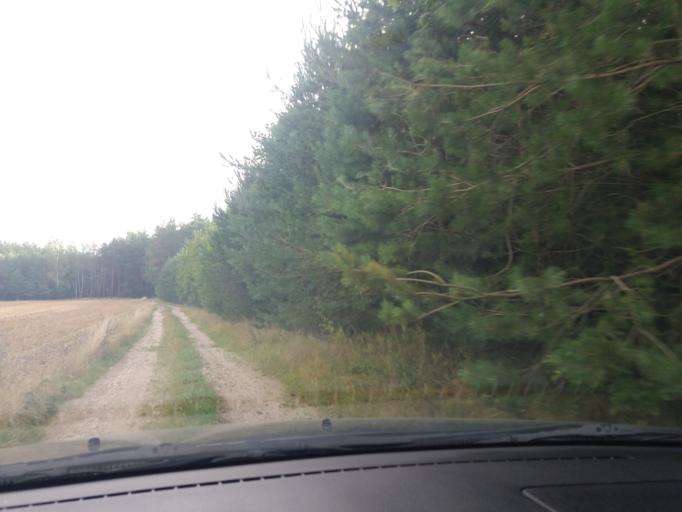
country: PL
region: Masovian Voivodeship
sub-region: Powiat mlawski
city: Wieczfnia Koscielna
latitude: 53.2182
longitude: 20.4576
